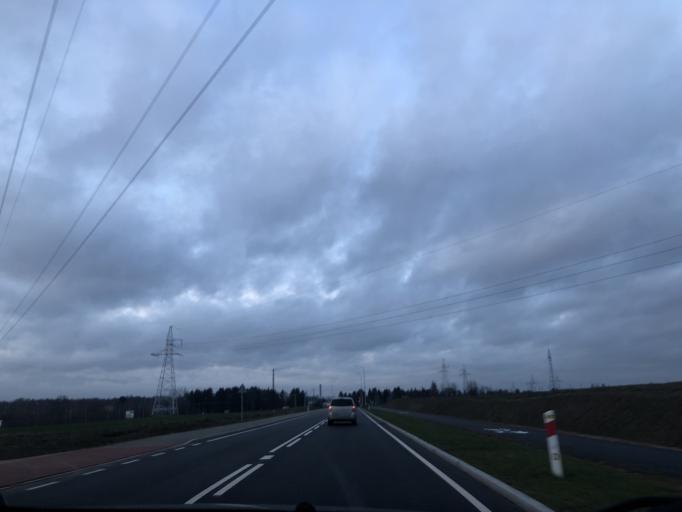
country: PL
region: Podlasie
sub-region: Lomza
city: Lomza
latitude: 53.1484
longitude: 22.0519
